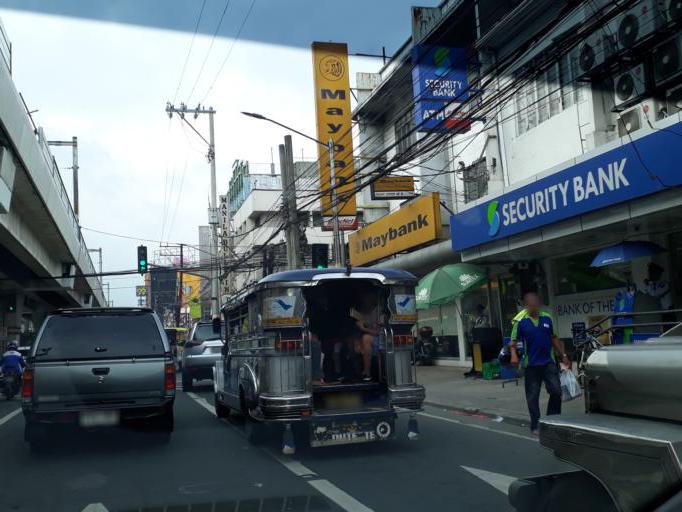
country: PH
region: Metro Manila
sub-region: Caloocan City
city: Niugan
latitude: 14.6512
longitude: 120.9840
